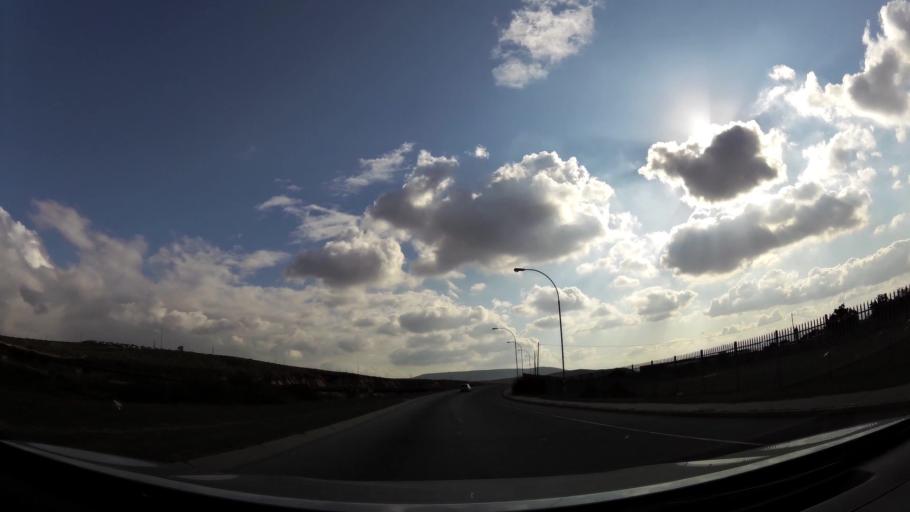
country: ZA
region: Eastern Cape
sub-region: Nelson Mandela Bay Metropolitan Municipality
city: Uitenhage
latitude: -33.7909
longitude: 25.4098
